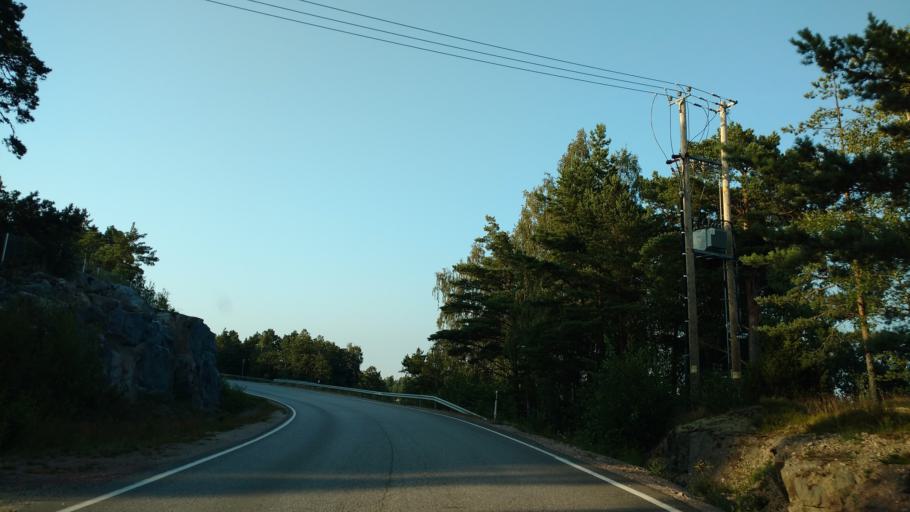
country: FI
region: Varsinais-Suomi
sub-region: Aboland-Turunmaa
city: Dragsfjaerd
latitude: 59.9802
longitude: 22.4514
